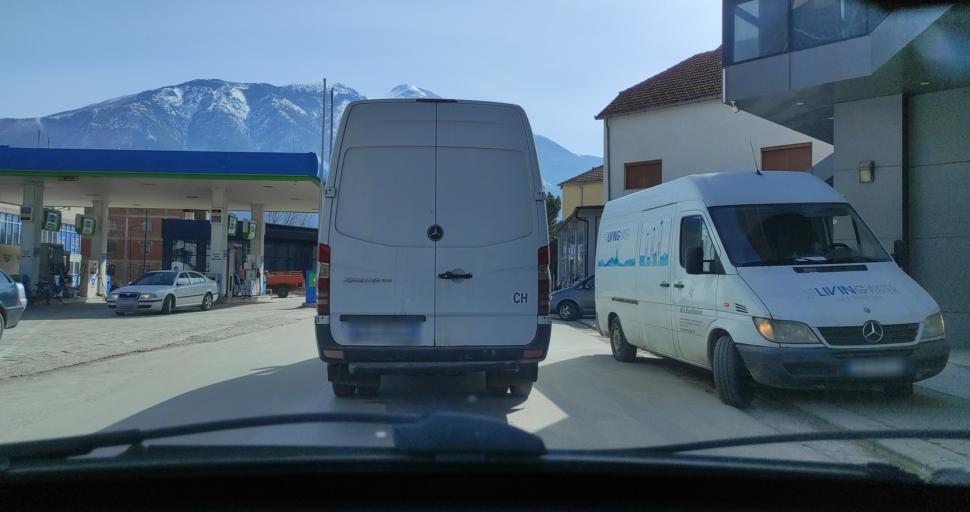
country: AL
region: Kukes
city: Kukes
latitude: 42.0767
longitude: 20.4253
